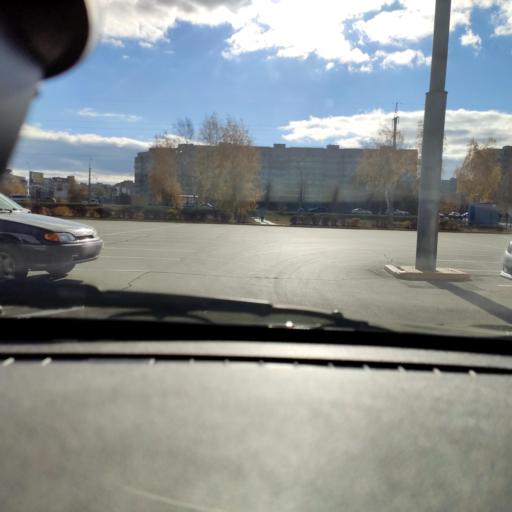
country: RU
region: Samara
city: Tol'yatti
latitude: 53.5482
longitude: 49.3603
